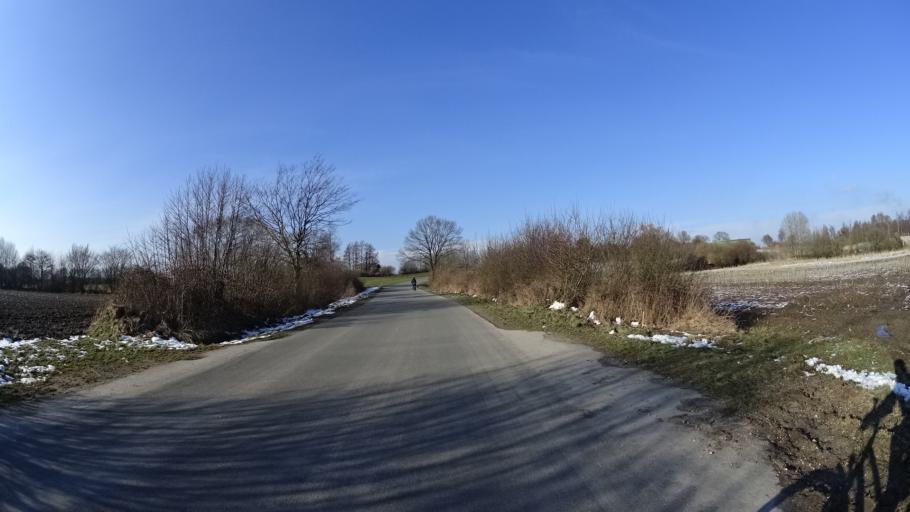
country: DE
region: Schleswig-Holstein
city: Martensrade
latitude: 54.2765
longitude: 10.3908
